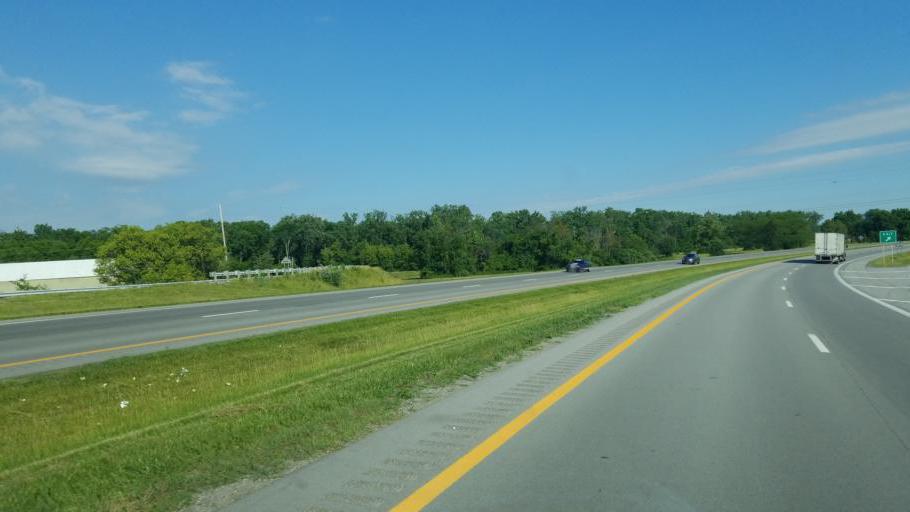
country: US
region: Ohio
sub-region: Hancock County
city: Findlay
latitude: 40.9882
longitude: -83.6481
